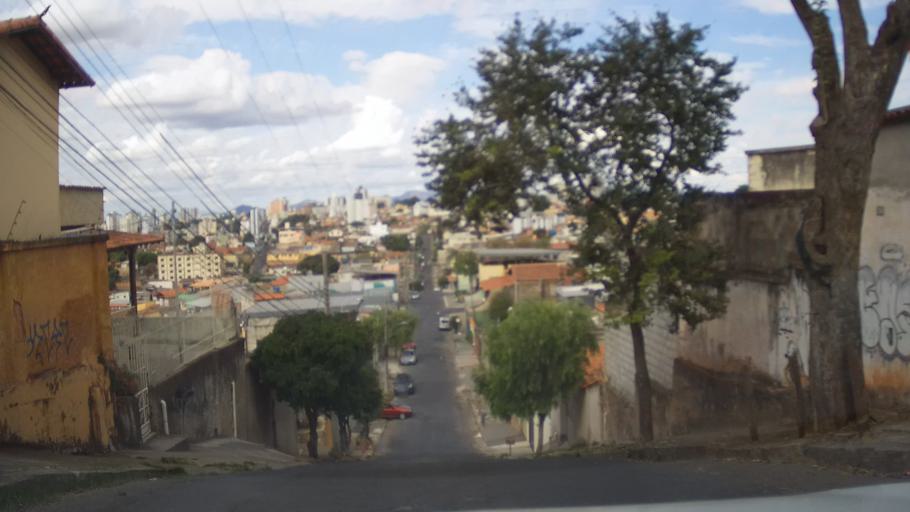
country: BR
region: Minas Gerais
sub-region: Belo Horizonte
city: Belo Horizonte
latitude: -19.9020
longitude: -43.9408
